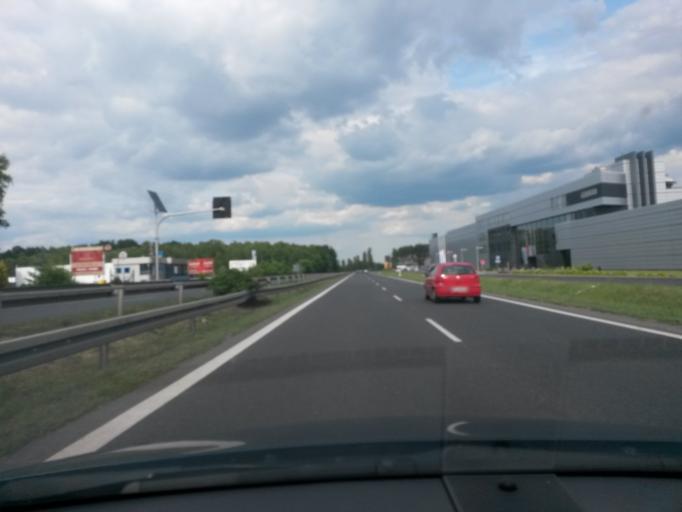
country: PL
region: Masovian Voivodeship
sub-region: Powiat pruszkowski
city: Nadarzyn
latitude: 52.0829
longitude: 20.7951
